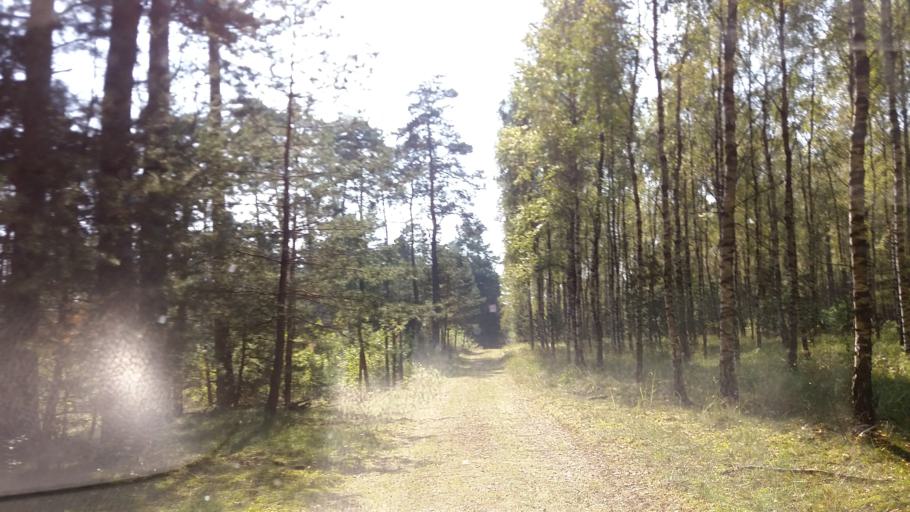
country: PL
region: West Pomeranian Voivodeship
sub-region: Powiat drawski
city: Kalisz Pomorski
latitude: 53.1204
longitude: 15.9361
